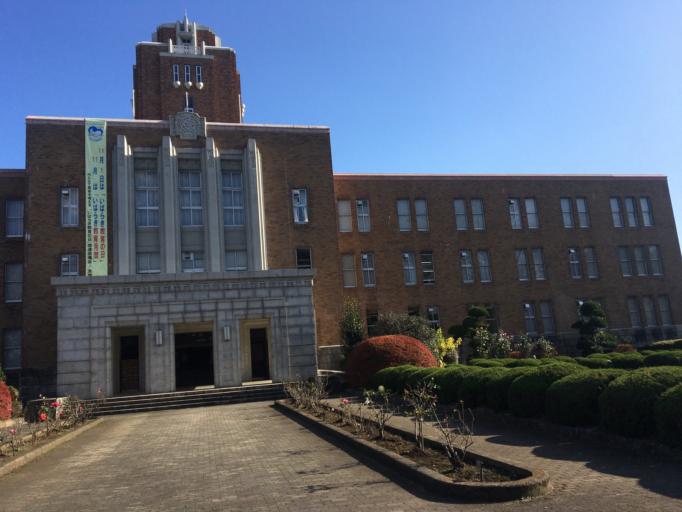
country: JP
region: Ibaraki
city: Mito-shi
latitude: 36.3765
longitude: 140.4752
